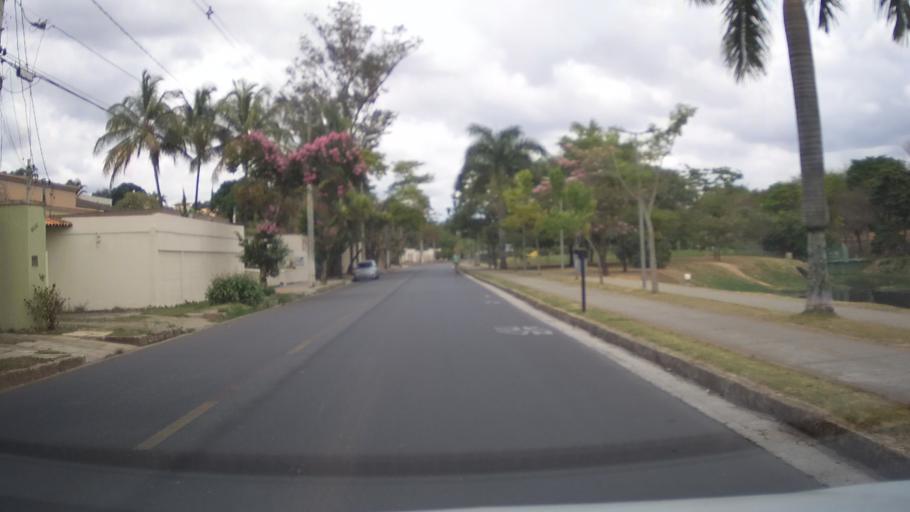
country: BR
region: Minas Gerais
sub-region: Belo Horizonte
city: Belo Horizonte
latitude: -19.8558
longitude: -43.9948
